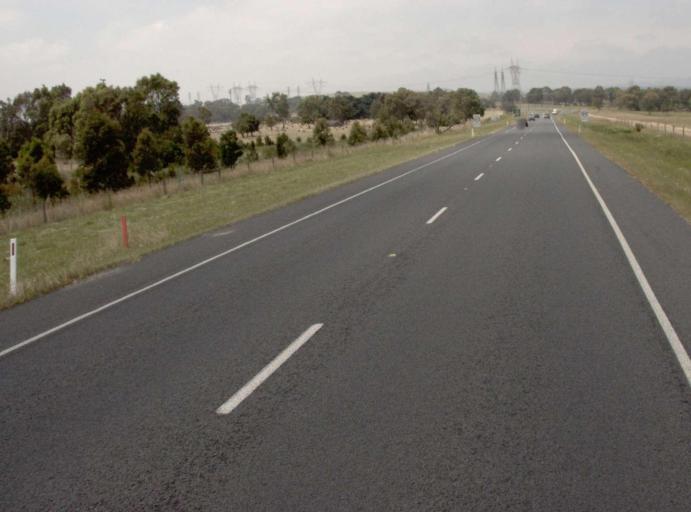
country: AU
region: Victoria
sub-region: Latrobe
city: Traralgon
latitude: -38.2434
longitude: 146.5457
